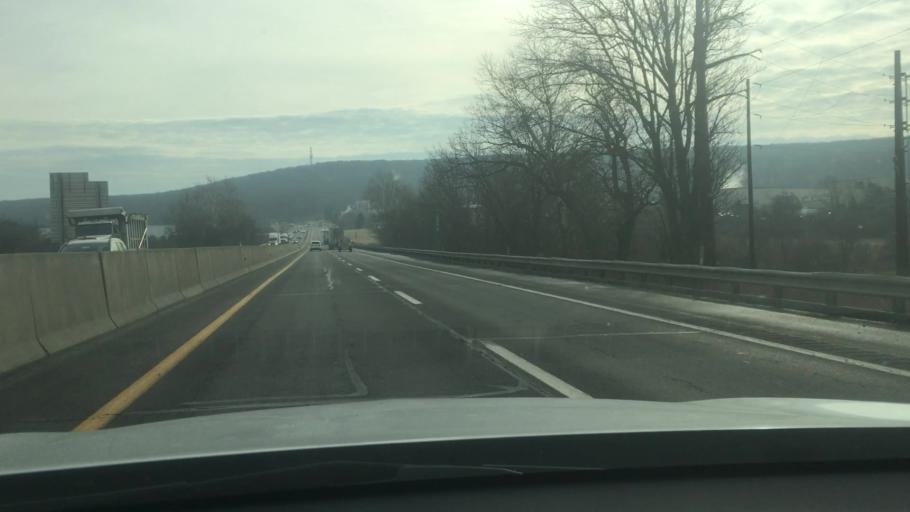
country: US
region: Pennsylvania
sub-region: Chester County
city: Elverson
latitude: 40.1524
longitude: -75.8644
